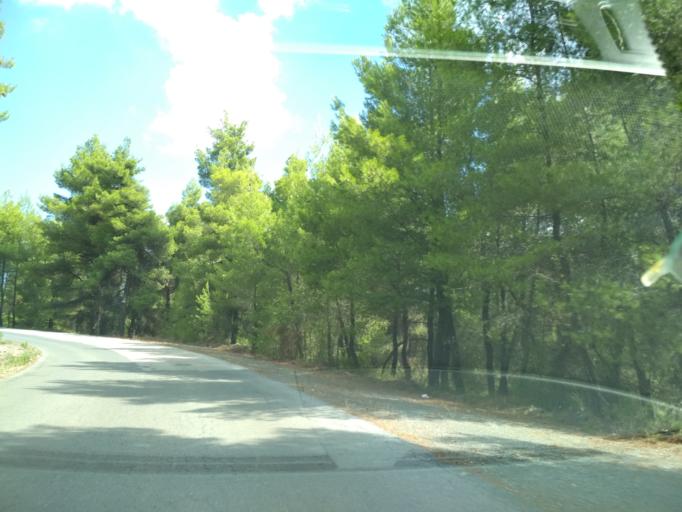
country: GR
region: Central Greece
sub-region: Nomos Evvoias
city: Roviai
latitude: 38.8378
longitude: 23.2859
